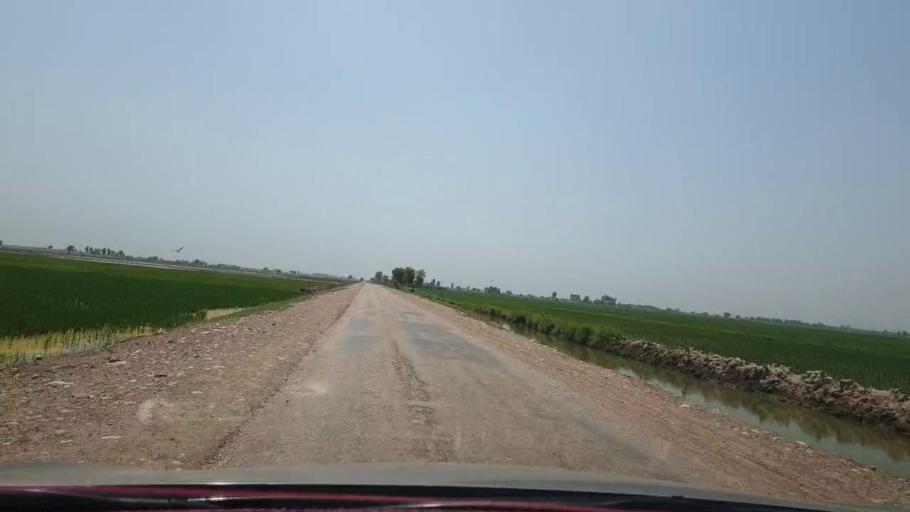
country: PK
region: Sindh
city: Warah
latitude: 27.5669
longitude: 67.8029
